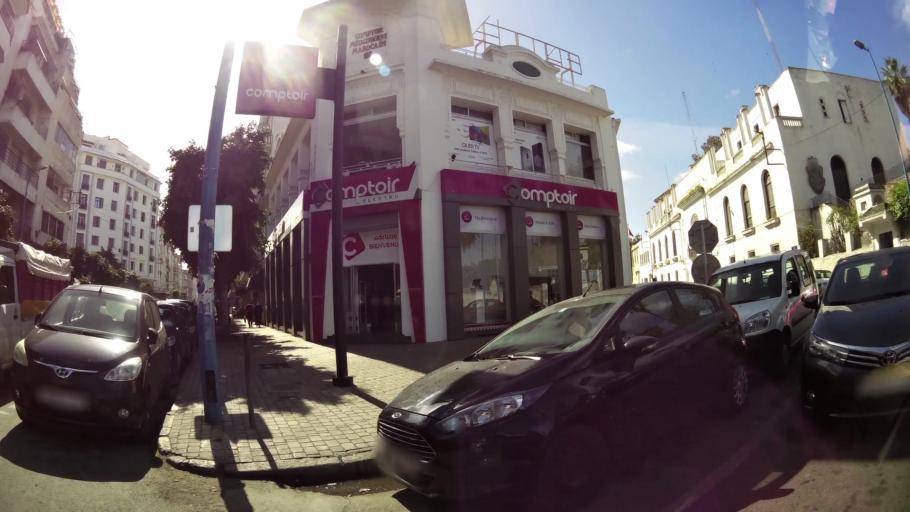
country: MA
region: Grand Casablanca
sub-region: Casablanca
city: Casablanca
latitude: 33.5923
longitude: -7.6171
